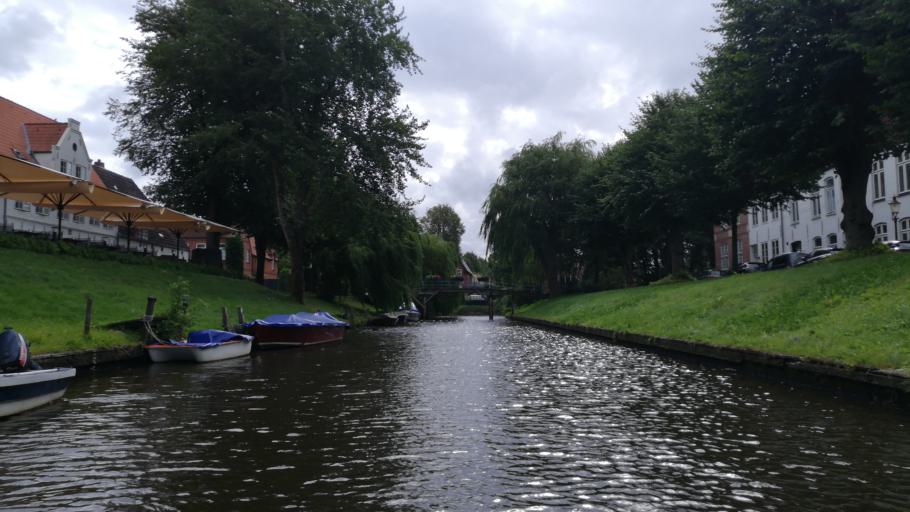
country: DE
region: Schleswig-Holstein
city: Friedrichstadt
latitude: 54.3764
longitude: 9.0899
